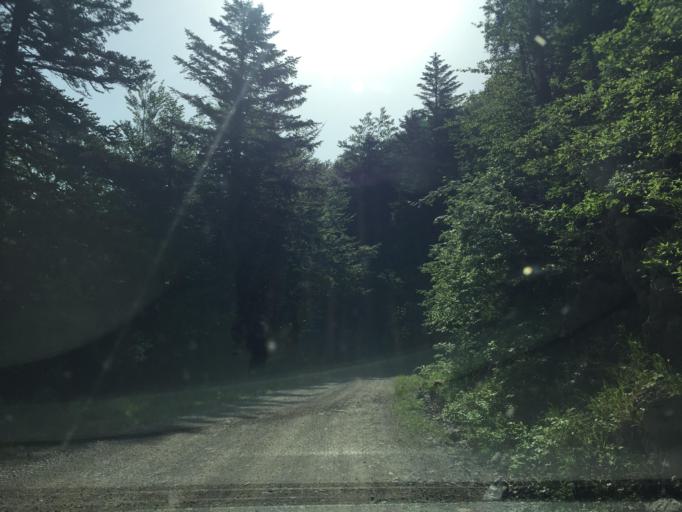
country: HR
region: Primorsko-Goranska
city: Podhum
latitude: 45.4525
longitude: 14.5462
